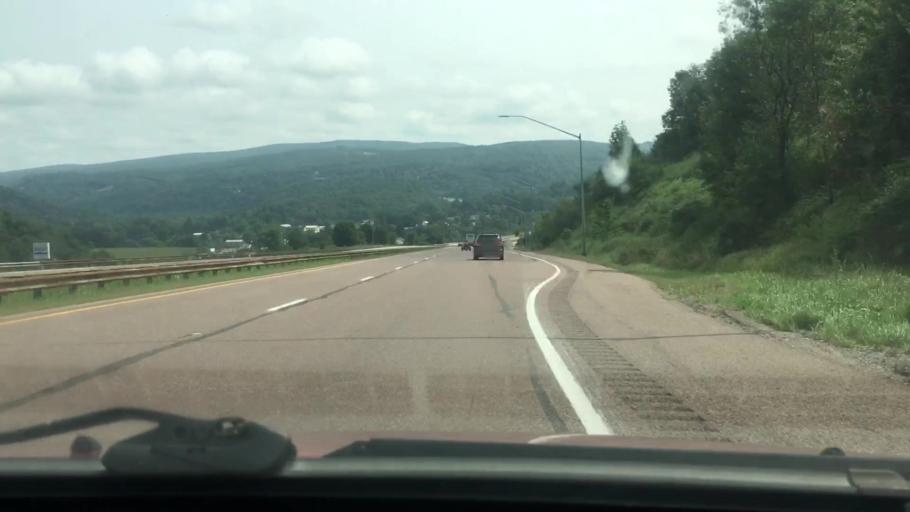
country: US
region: West Virginia
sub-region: Preston County
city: Terra Alta
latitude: 39.6620
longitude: -79.4189
